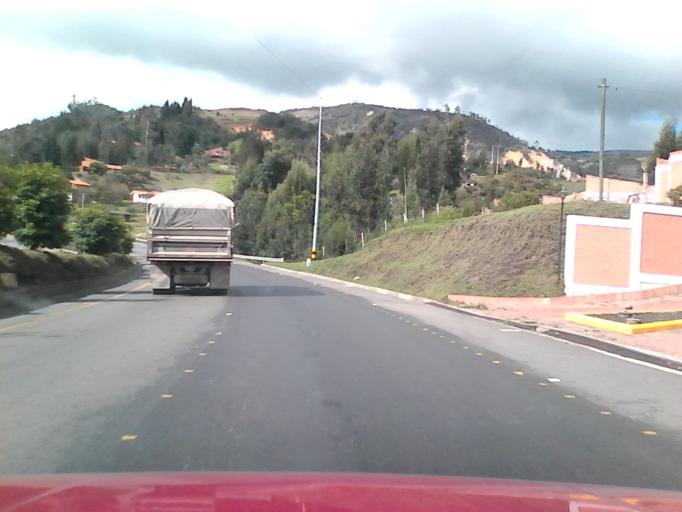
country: CO
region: Boyaca
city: Combita
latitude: 5.6138
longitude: -73.3231
